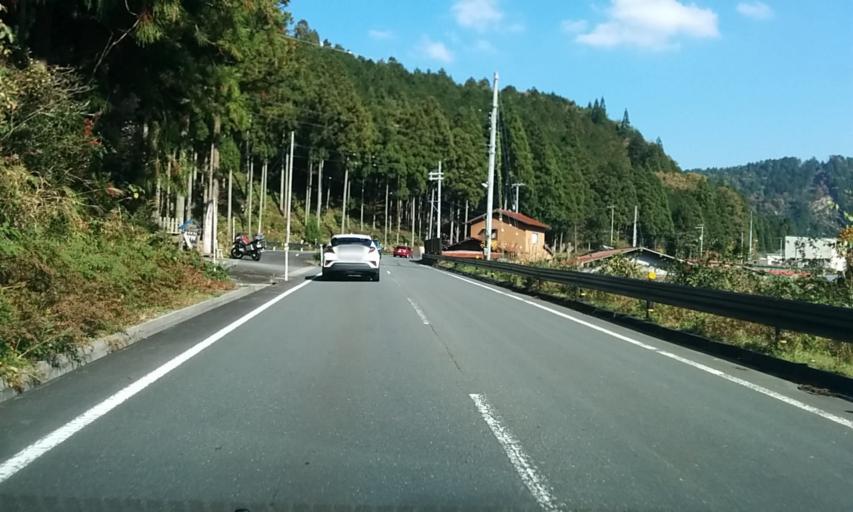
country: JP
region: Fukui
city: Obama
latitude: 35.3038
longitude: 135.6162
